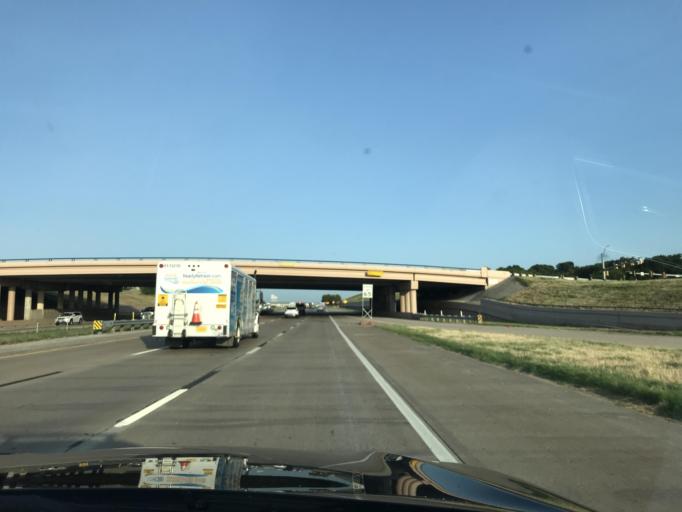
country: US
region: Texas
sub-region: Tarrant County
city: Benbrook
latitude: 32.6836
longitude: -97.4126
